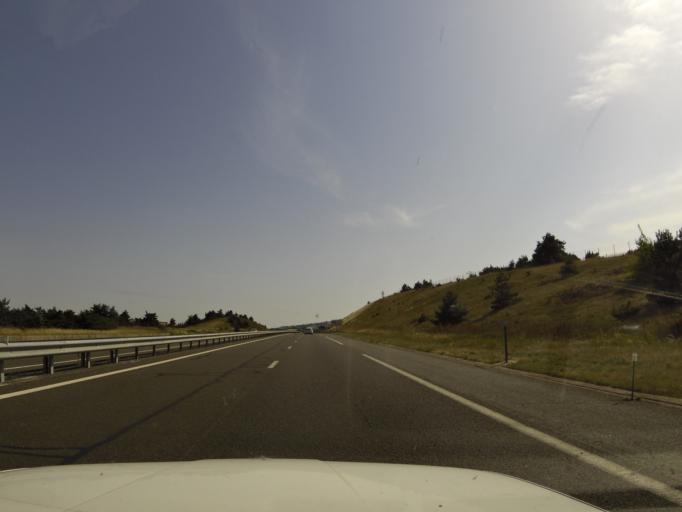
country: FR
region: Midi-Pyrenees
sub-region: Departement de l'Aveyron
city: Severac-le-Chateau
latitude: 44.3009
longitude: 3.1012
